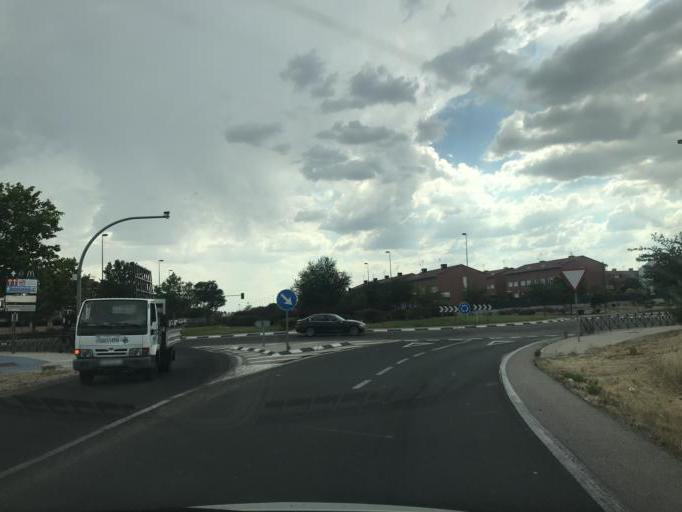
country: ES
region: Madrid
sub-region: Provincia de Madrid
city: Paracuellos de Jarama
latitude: 40.5108
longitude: -3.5132
